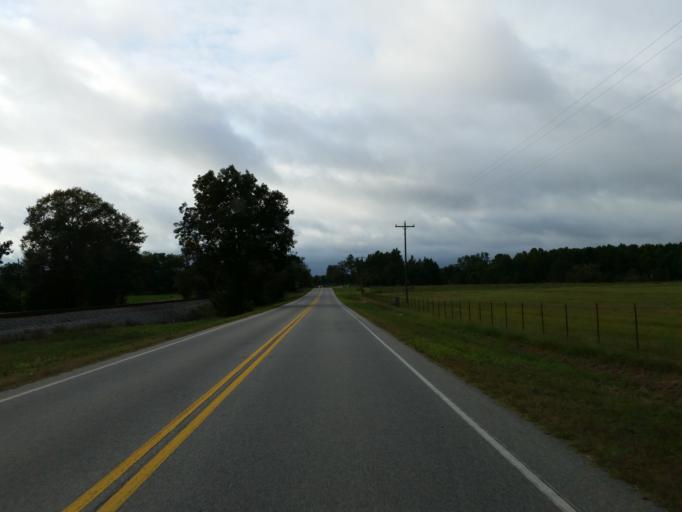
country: US
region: Georgia
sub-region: Turner County
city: Ashburn
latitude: 31.5926
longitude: -83.5807
